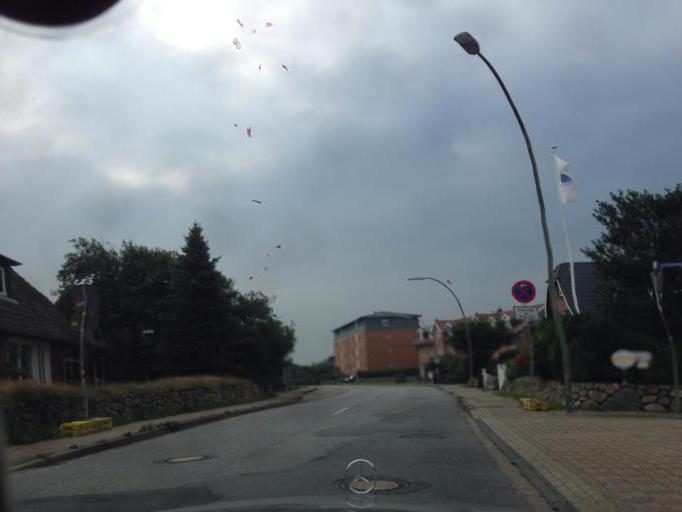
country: DE
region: Schleswig-Holstein
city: Westerland
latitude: 54.8988
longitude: 8.3049
